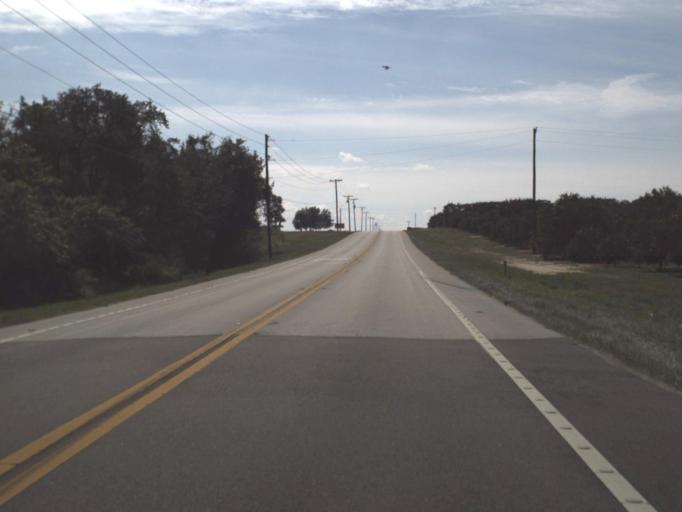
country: US
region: Florida
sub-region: Highlands County
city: Sebring
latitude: 27.5402
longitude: -81.4534
